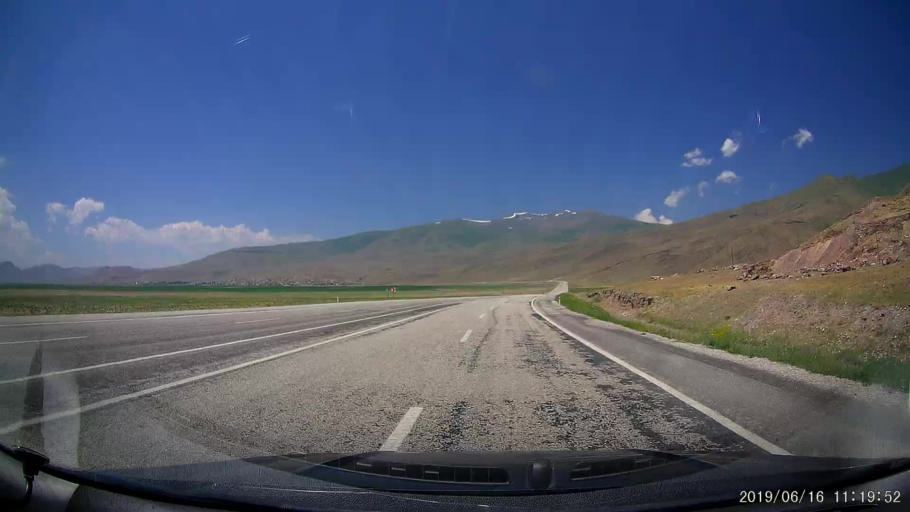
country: TR
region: Agri
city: Dogubayazit
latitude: 39.6958
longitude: 44.1049
